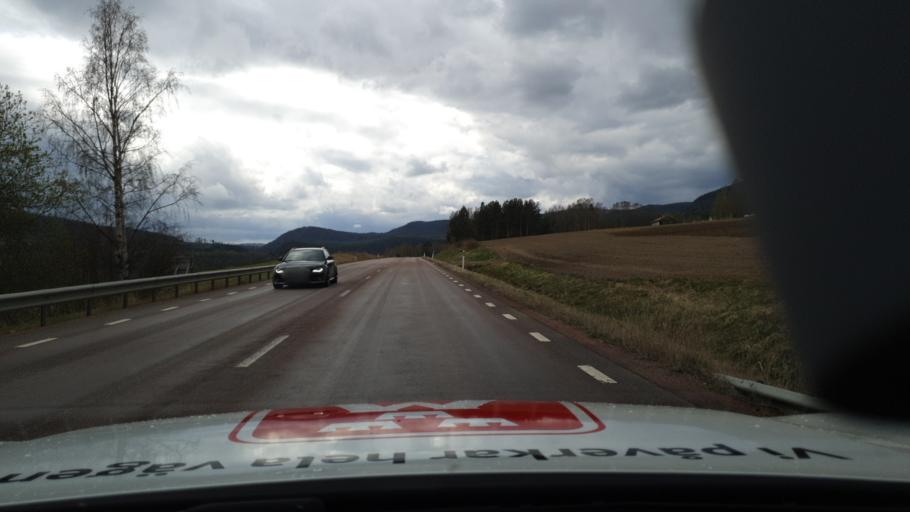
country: SE
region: Jaemtland
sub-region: Ragunda Kommun
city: Hammarstrand
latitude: 63.1466
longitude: 16.1449
